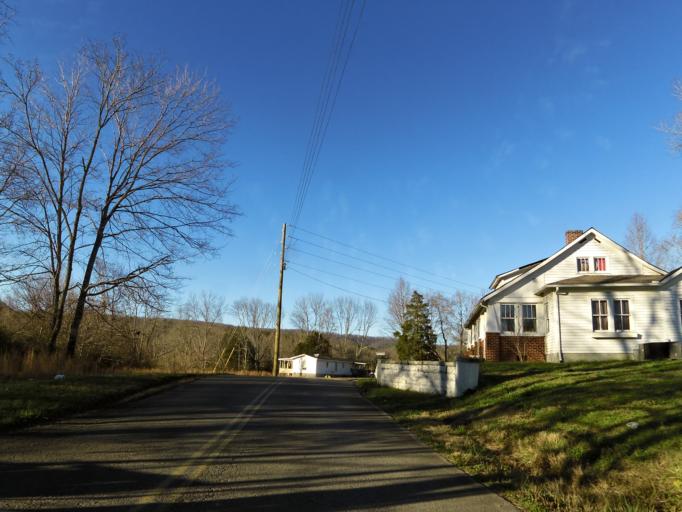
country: US
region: Tennessee
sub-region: Anderson County
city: Oak Ridge
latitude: 36.0599
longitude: -84.2457
